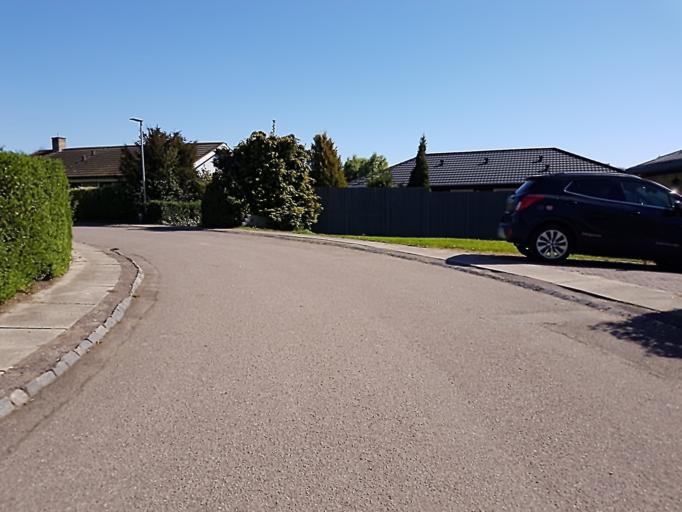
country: DK
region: Capital Region
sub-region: Egedal Kommune
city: Olstykke
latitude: 55.7921
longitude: 12.1392
